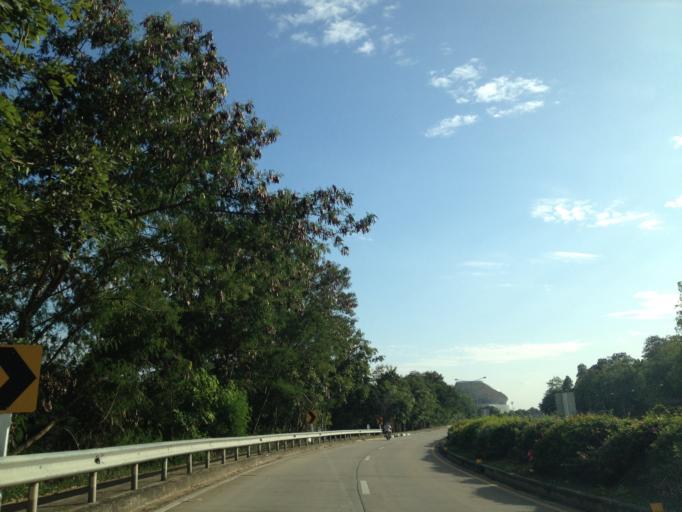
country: TH
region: Chiang Mai
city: Chiang Mai
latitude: 18.8566
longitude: 98.9625
